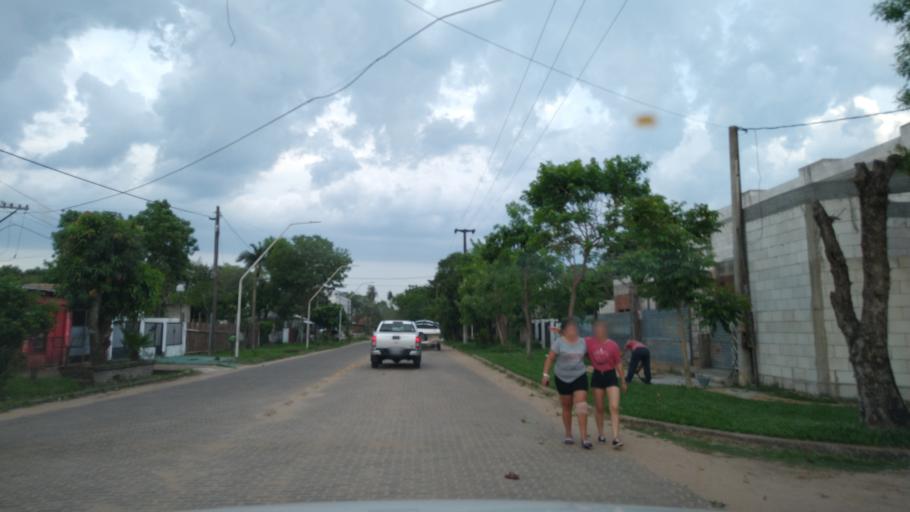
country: AR
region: Corrientes
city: Ituzaingo
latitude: -27.5886
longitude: -56.6976
